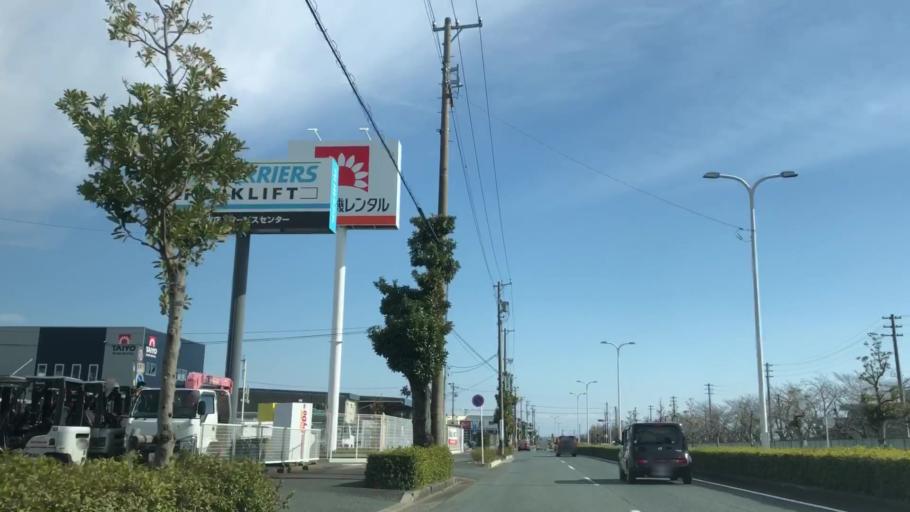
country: JP
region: Shizuoka
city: Hamamatsu
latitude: 34.7555
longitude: 137.6966
